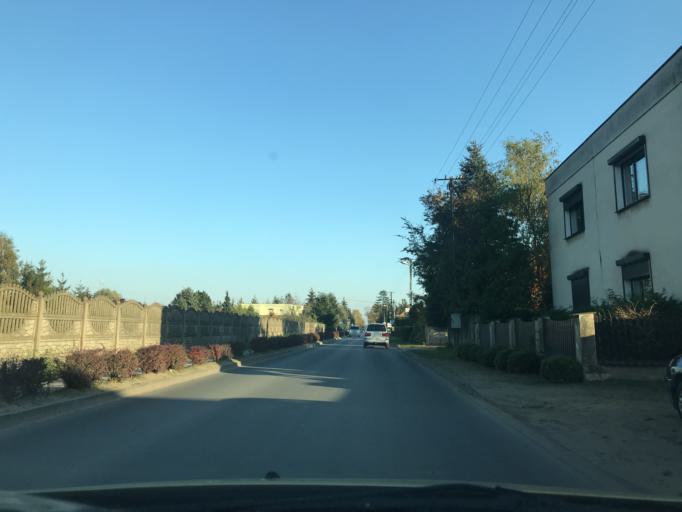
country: PL
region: Greater Poland Voivodeship
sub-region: Powiat poznanski
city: Baranowo
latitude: 52.3991
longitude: 16.7503
